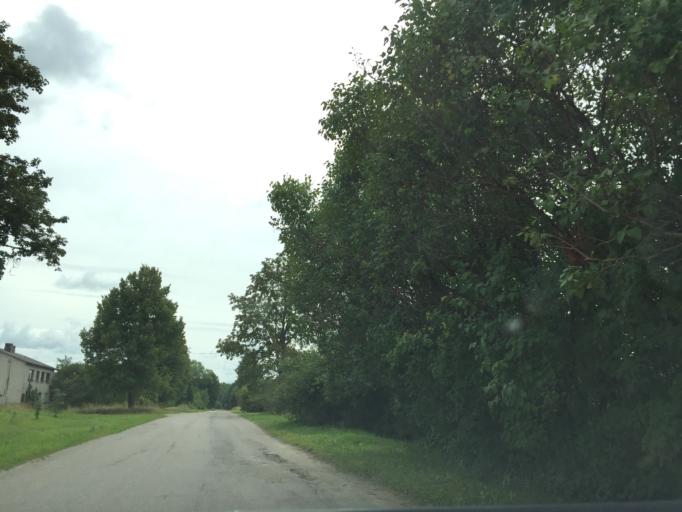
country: LV
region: Lielvarde
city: Lielvarde
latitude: 56.7576
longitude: 24.8425
